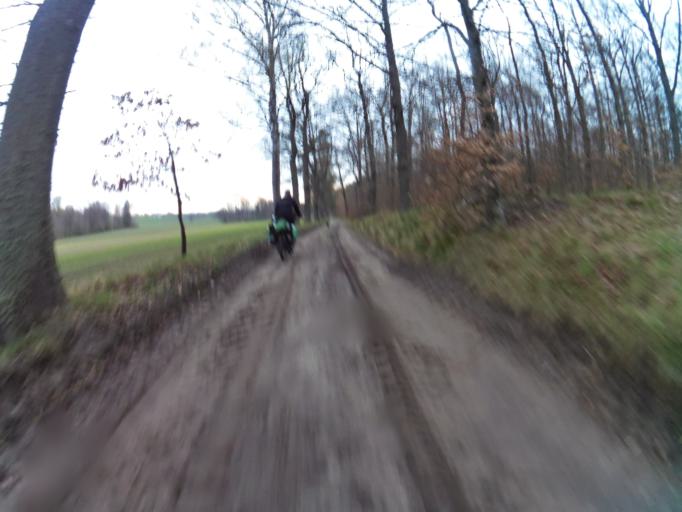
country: PL
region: West Pomeranian Voivodeship
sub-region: Powiat szczecinecki
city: Borne Sulinowo
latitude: 53.6675
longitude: 16.5412
